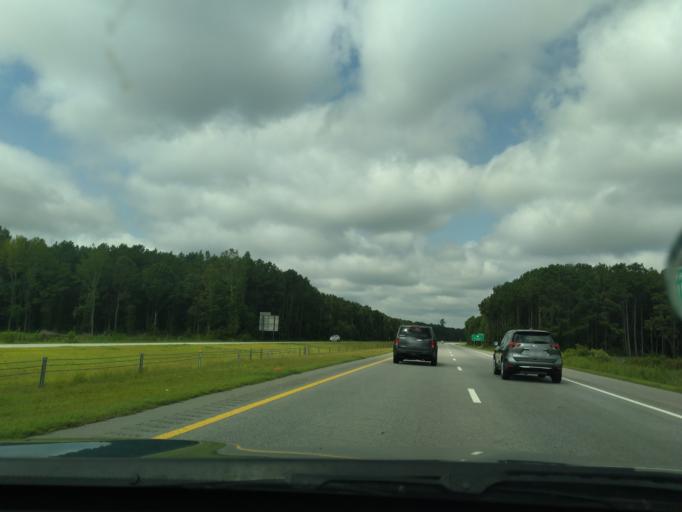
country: US
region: North Carolina
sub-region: Martin County
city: Williamston
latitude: 35.8178
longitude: -77.0854
